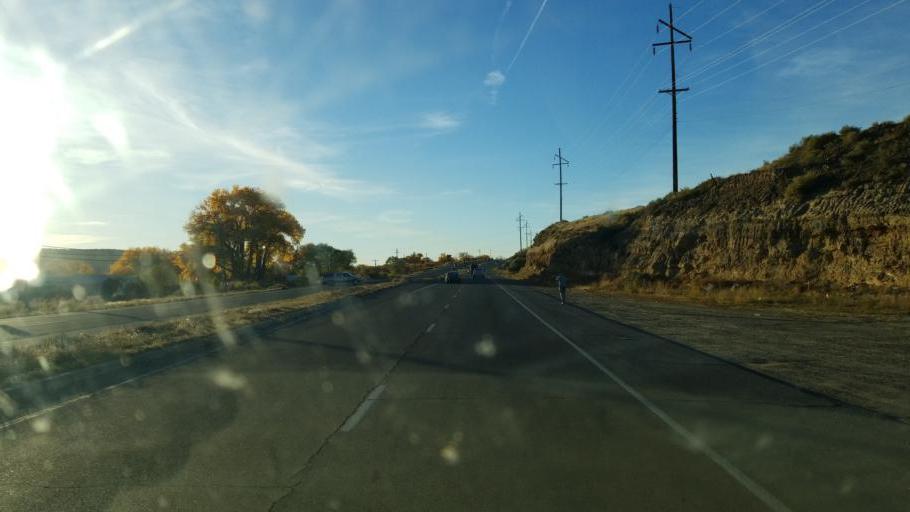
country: US
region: New Mexico
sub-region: San Juan County
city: Farmington
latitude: 36.7105
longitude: -108.1372
